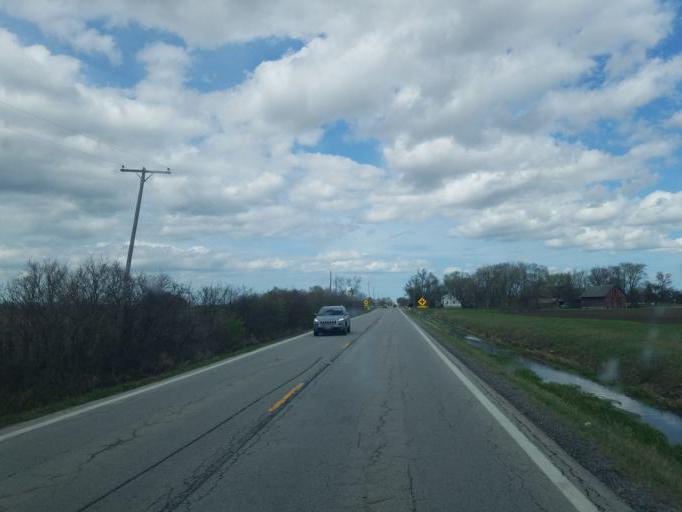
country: US
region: Ohio
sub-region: Huron County
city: Bellevue
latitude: 41.3222
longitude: -82.7679
